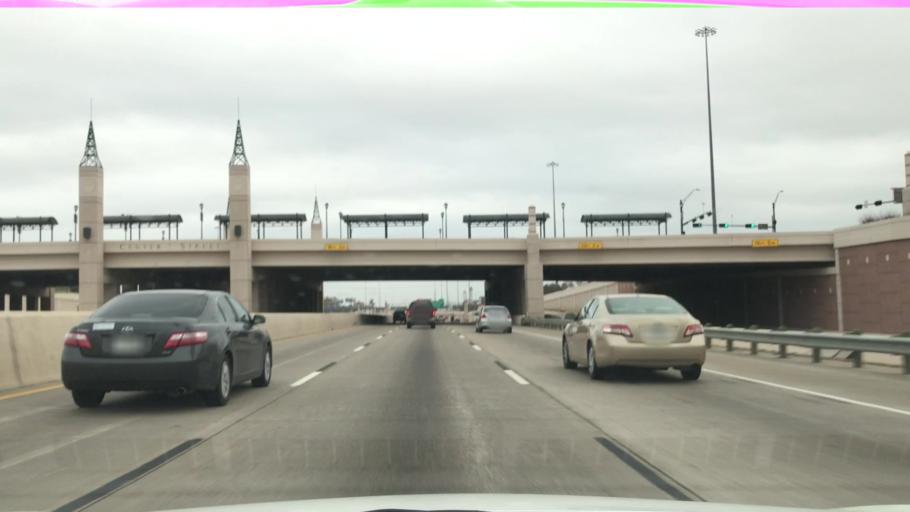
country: US
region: Texas
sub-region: Tarrant County
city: Arlington
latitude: 32.7595
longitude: -97.1031
